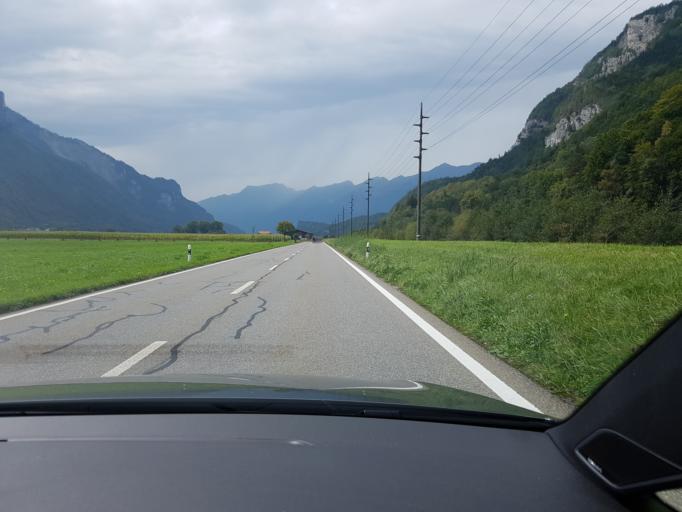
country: CH
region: Obwalden
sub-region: Obwalden
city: Lungern
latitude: 46.7439
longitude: 8.1319
